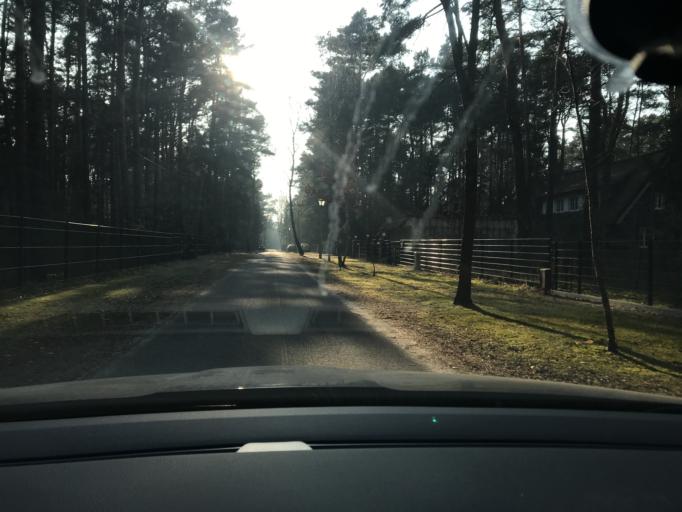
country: DE
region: Brandenburg
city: Munchehofe
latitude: 52.2148
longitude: 13.7937
